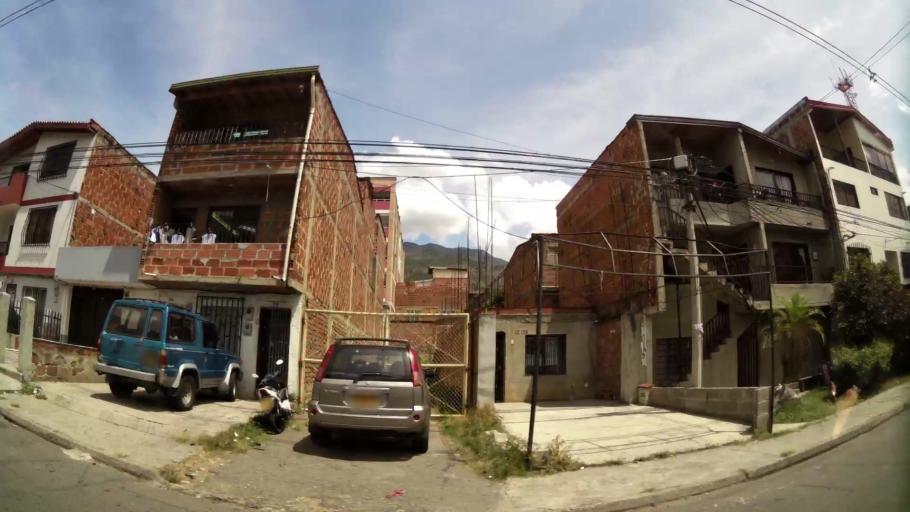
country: CO
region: Antioquia
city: Bello
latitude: 6.3403
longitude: -75.5495
